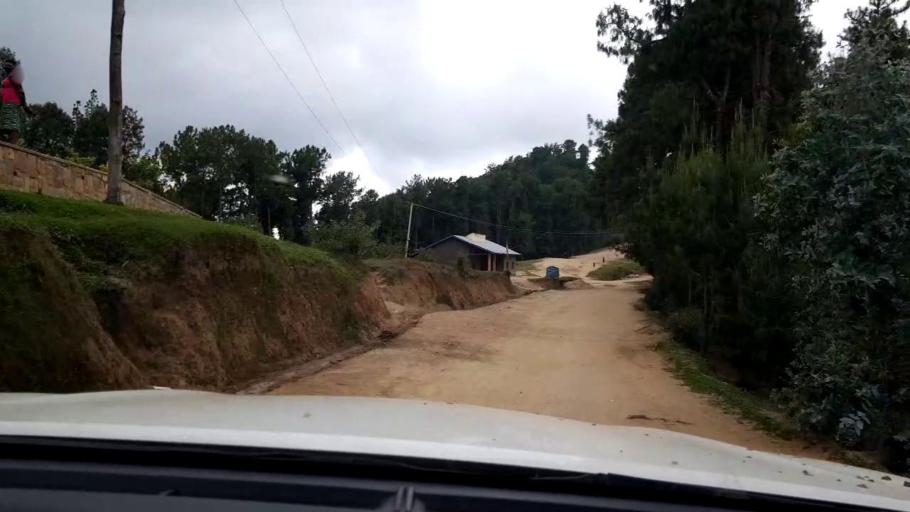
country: RW
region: Western Province
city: Kibuye
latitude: -1.8915
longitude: 29.5273
